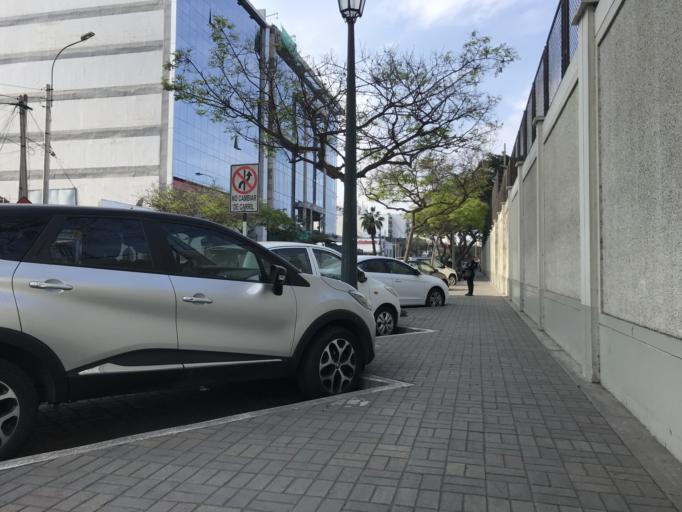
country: PE
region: Lima
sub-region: Lima
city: San Isidro
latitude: -12.1083
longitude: -77.0370
